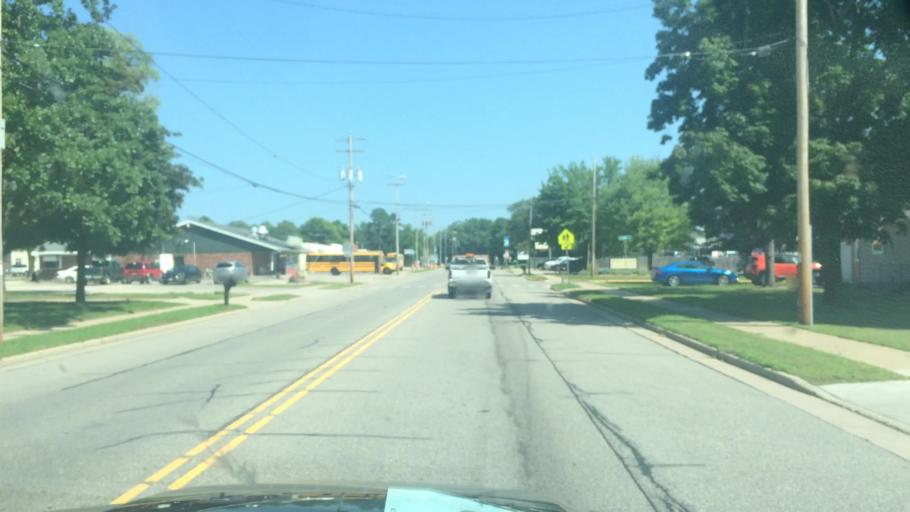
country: US
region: Wisconsin
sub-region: Waupaca County
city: Waupaca
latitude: 44.3481
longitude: -89.0721
